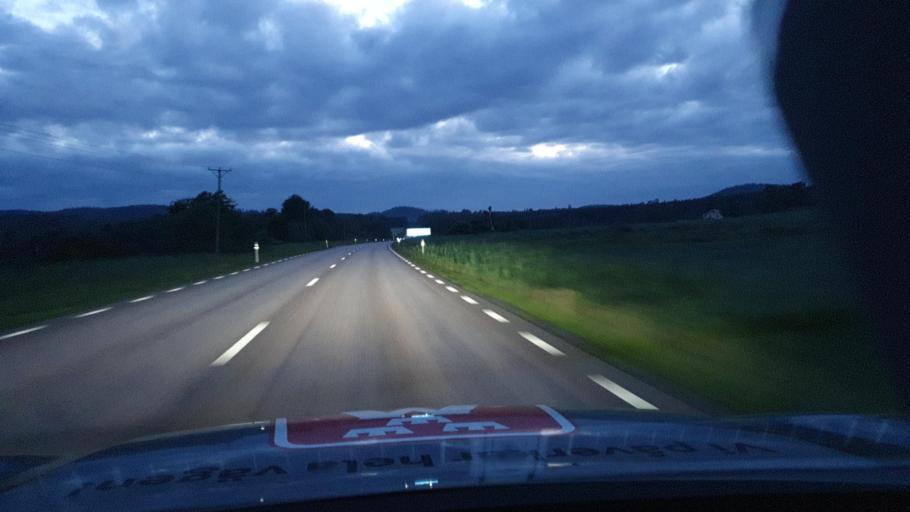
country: SE
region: OErebro
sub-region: Karlskoga Kommun
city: Karlskoga
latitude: 59.4350
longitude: 14.4117
